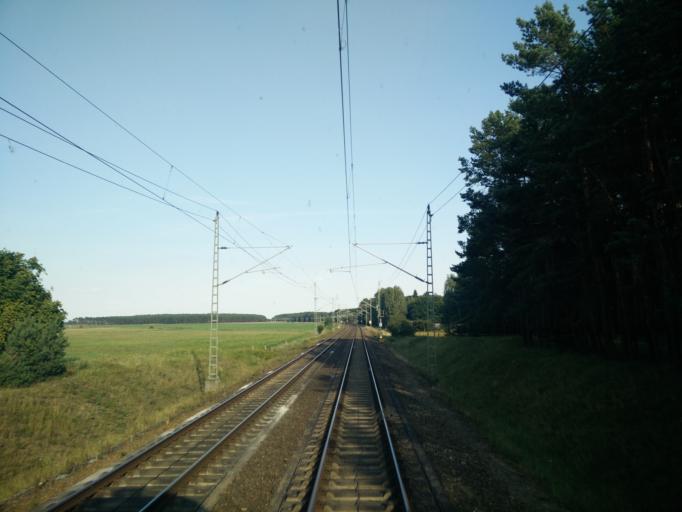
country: DE
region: Saxony-Anhalt
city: Havelberg
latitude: 52.8931
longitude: 12.1324
